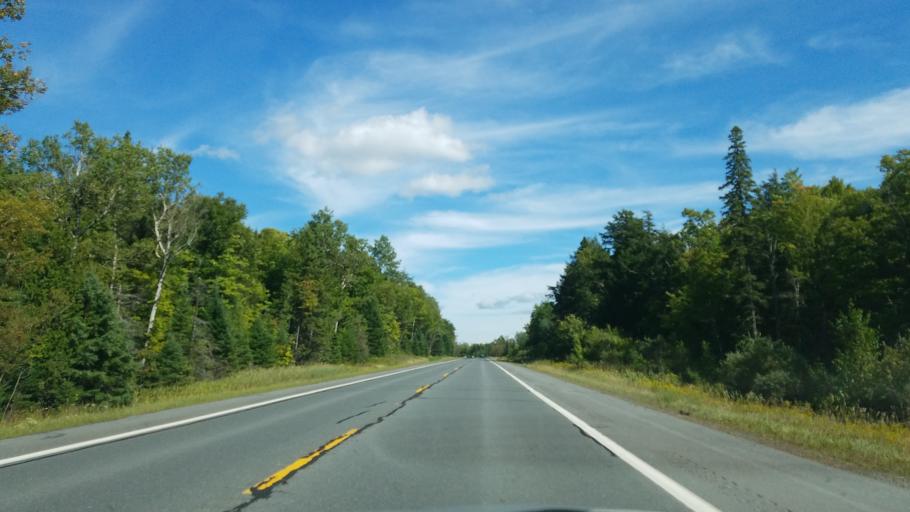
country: US
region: Michigan
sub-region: Baraga County
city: L'Anse
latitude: 46.5804
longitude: -88.4586
